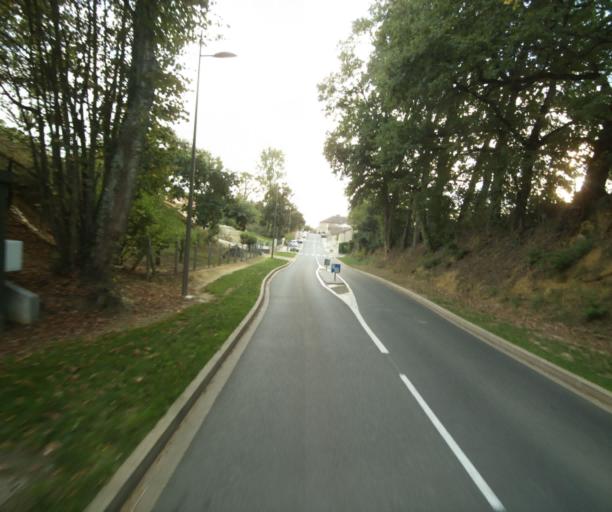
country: FR
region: Aquitaine
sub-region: Departement des Landes
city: Gabarret
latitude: 43.9499
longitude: 0.0874
